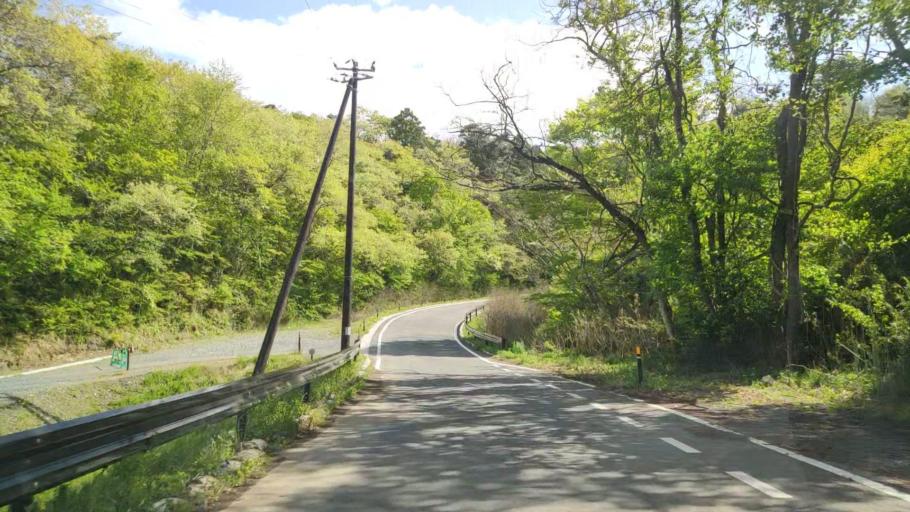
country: JP
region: Miyagi
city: Matsushima
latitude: 38.3409
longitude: 141.1557
